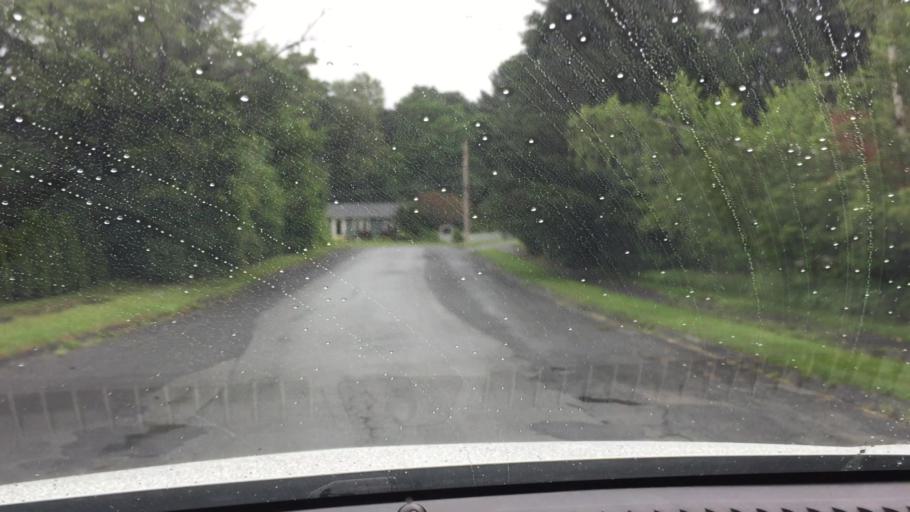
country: US
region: Massachusetts
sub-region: Berkshire County
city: Pittsfield
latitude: 42.4297
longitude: -73.2152
